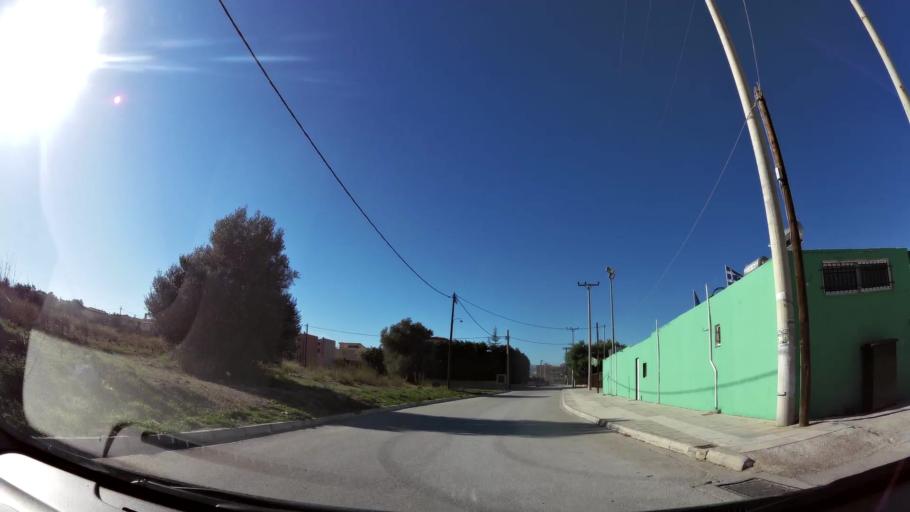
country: GR
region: Attica
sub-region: Nomarchia Anatolikis Attikis
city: Kalyvia Thorikou
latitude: 37.8352
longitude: 23.9337
